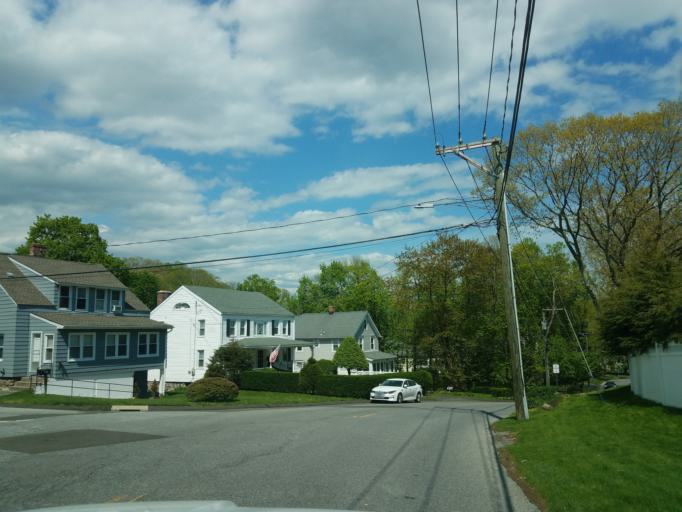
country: US
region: Connecticut
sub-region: Fairfield County
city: New Canaan
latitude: 41.1443
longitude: -73.4872
